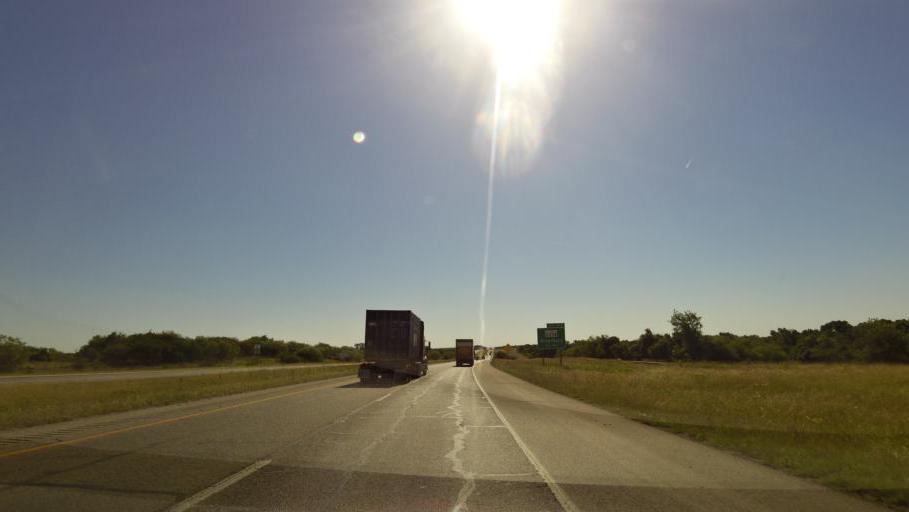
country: US
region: Texas
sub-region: Guadalupe County
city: Seguin
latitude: 29.6145
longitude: -97.8494
